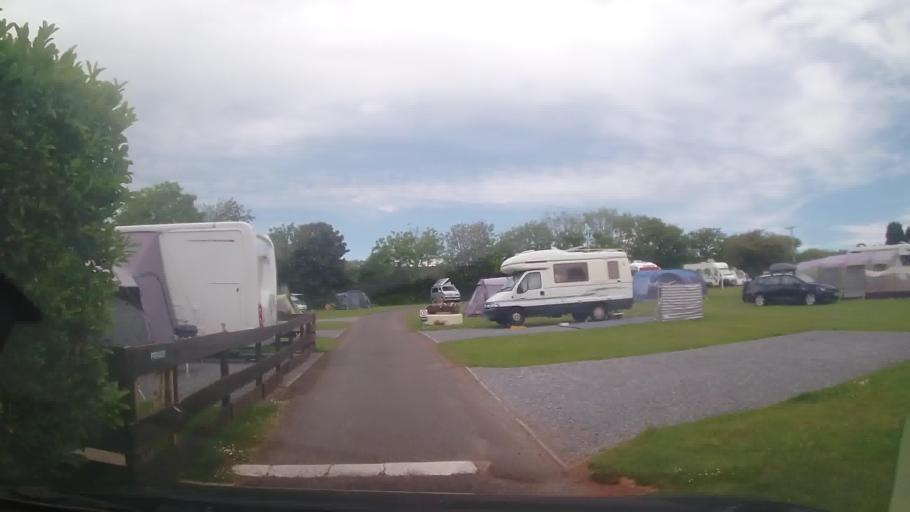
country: GB
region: England
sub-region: Devon
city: Dartmouth
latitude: 50.2911
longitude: -3.6509
